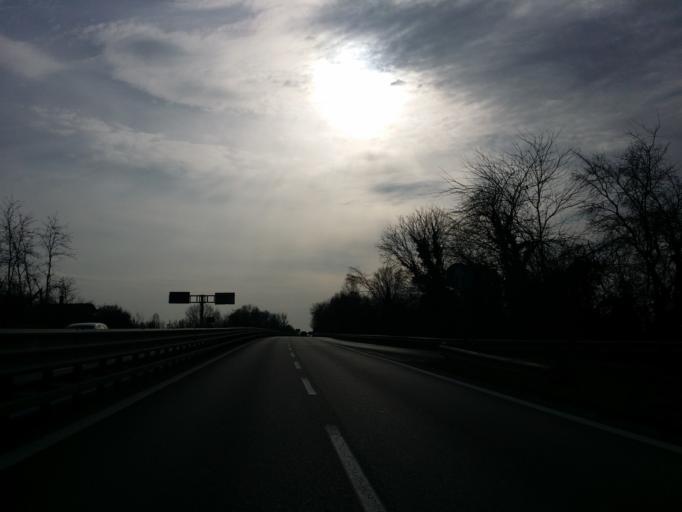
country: IT
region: Veneto
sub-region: Provincia di Padova
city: Mandriola-Sant'Agostino
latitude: 45.3947
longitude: 11.8415
